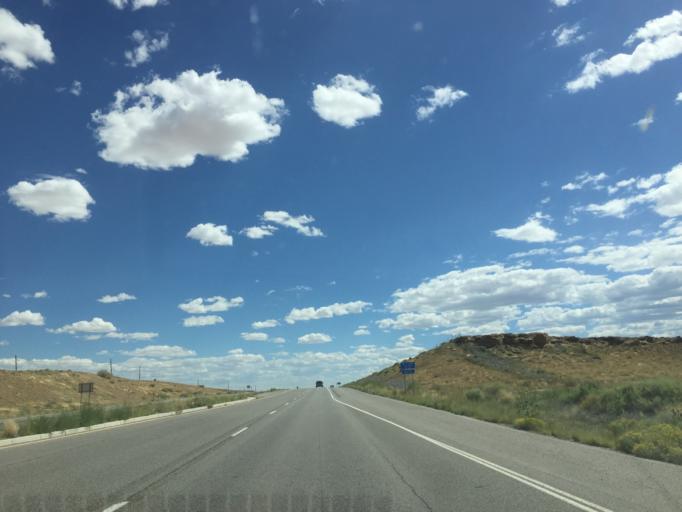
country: US
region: New Mexico
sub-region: San Juan County
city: Shiprock
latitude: 36.3320
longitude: -108.7118
